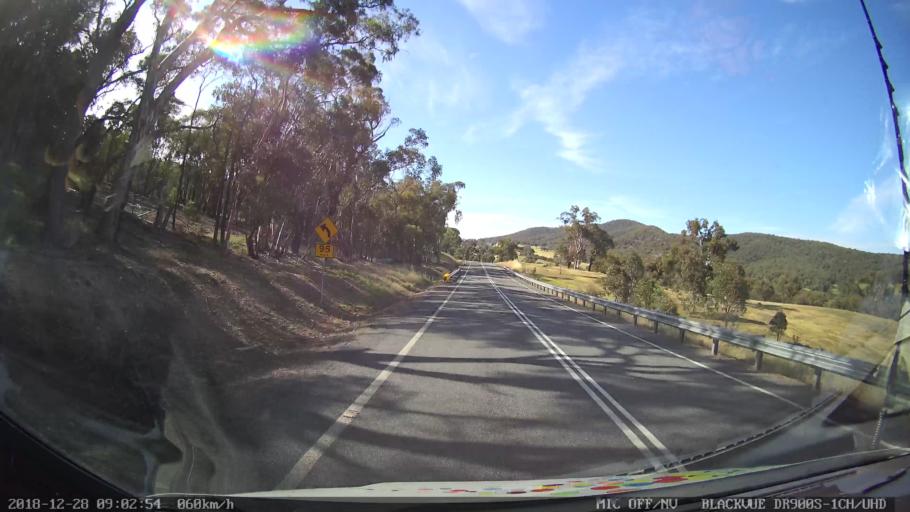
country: AU
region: New South Wales
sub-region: Upper Lachlan Shire
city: Crookwell
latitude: -34.1584
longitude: 149.3352
